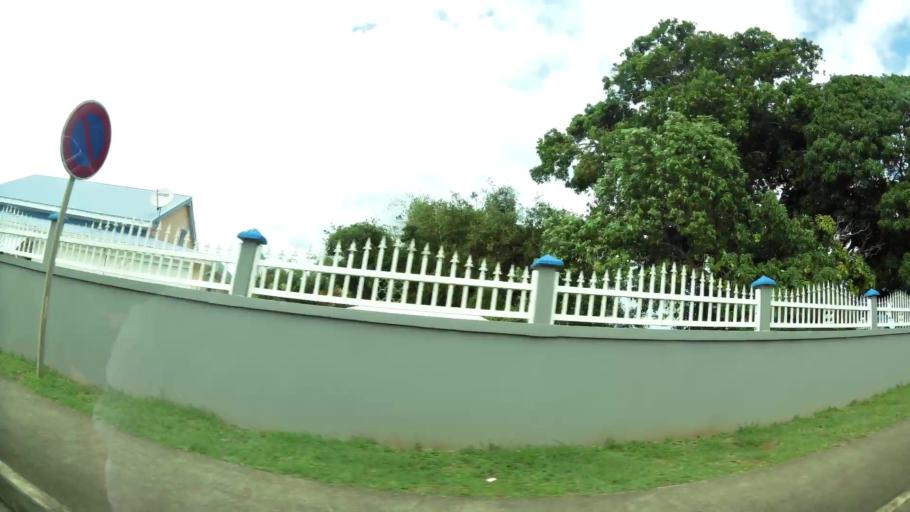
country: GP
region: Guadeloupe
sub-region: Guadeloupe
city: Baie-Mahault
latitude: 16.2596
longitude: -61.5961
